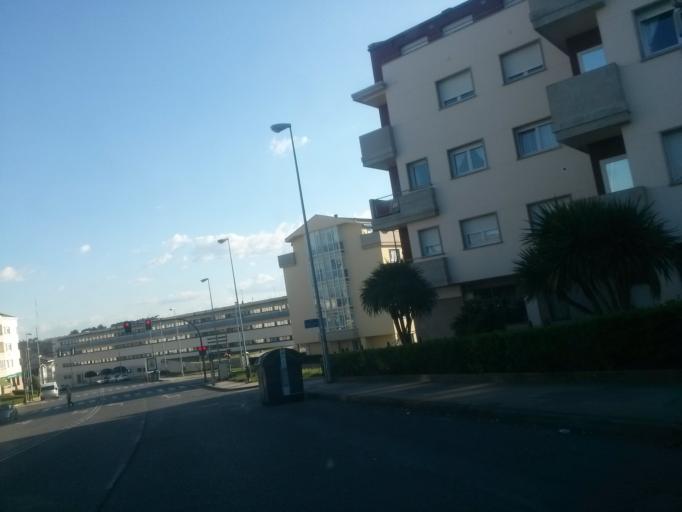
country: ES
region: Galicia
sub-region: Provincia de Lugo
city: Lugo
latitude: 42.9967
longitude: -7.5551
